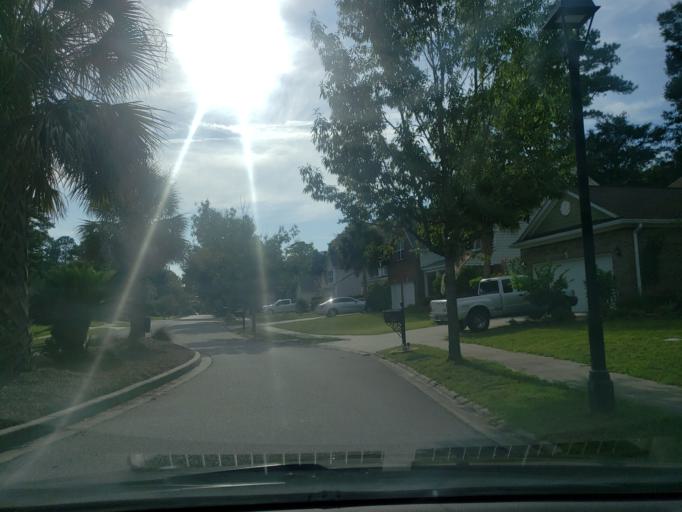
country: US
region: Georgia
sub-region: Chatham County
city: Montgomery
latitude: 31.9559
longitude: -81.1496
